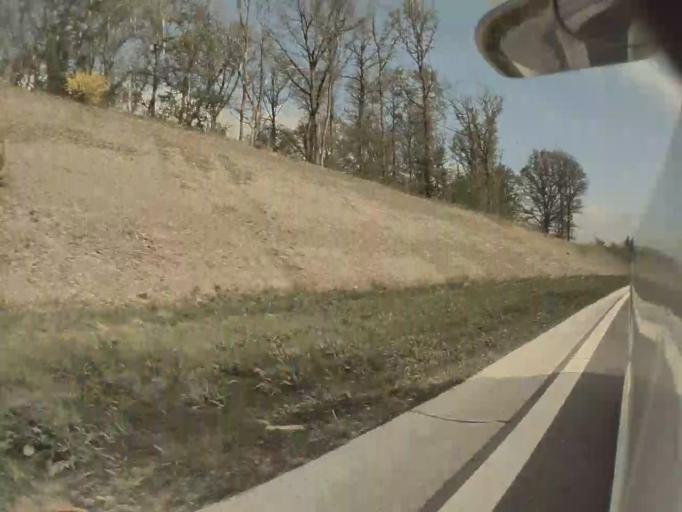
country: BE
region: Wallonia
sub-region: Province du Luxembourg
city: Marche-en-Famenne
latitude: 50.2243
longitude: 5.3146
